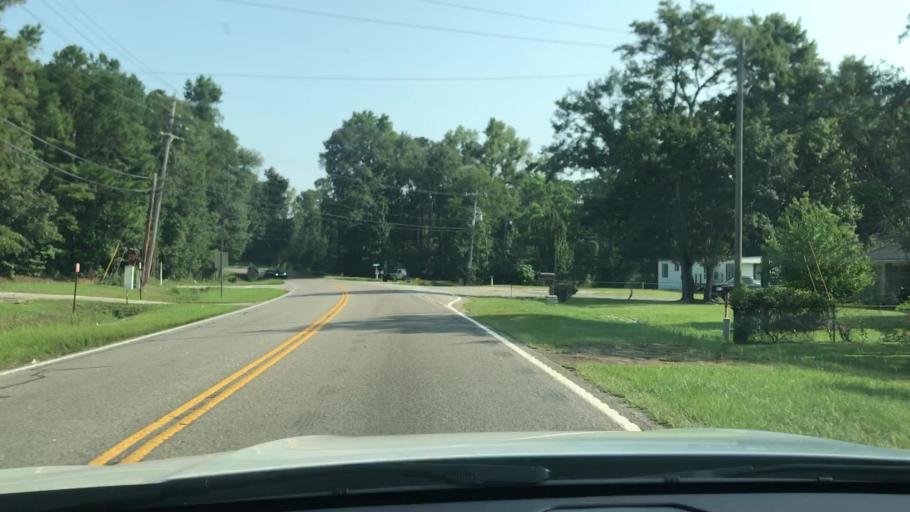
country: US
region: South Carolina
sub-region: Georgetown County
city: Georgetown
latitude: 33.4364
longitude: -79.2764
